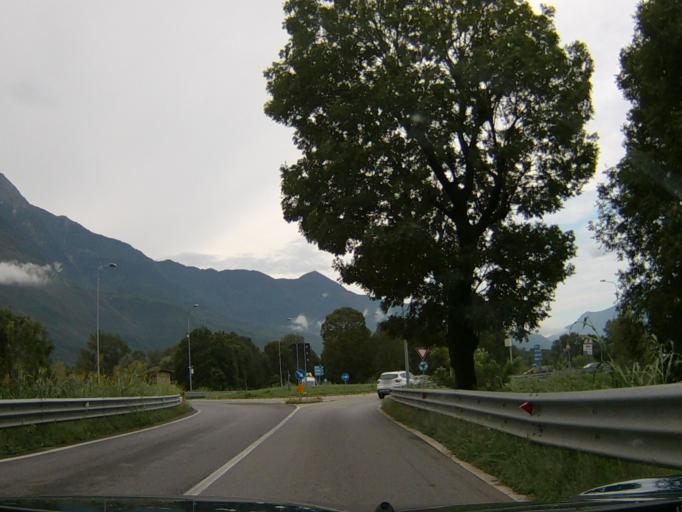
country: IT
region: Lombardy
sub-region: Provincia di Sondrio
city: Dubino
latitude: 46.1575
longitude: 9.4191
